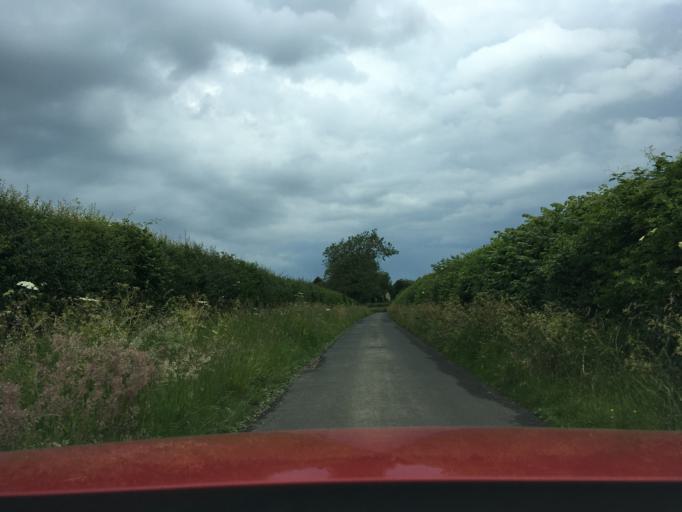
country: GB
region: England
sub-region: Gloucestershire
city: Shurdington
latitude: 51.8076
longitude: -2.0865
